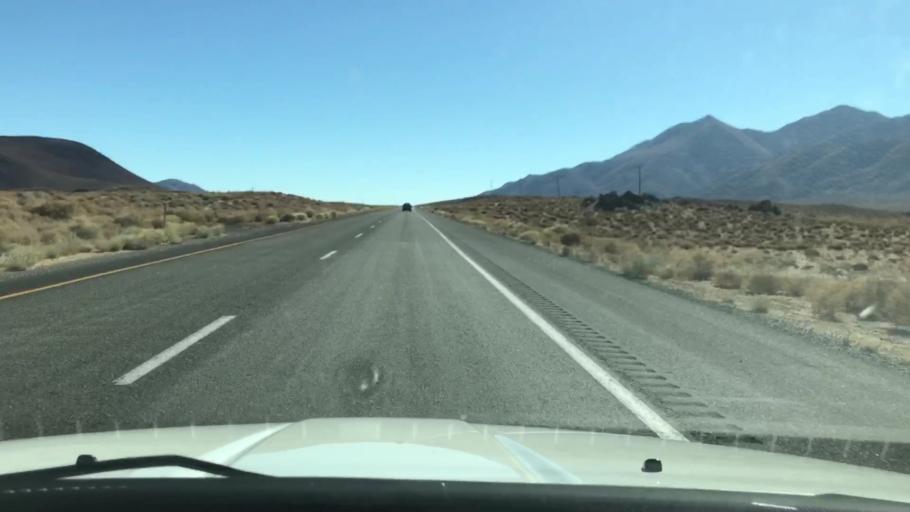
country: US
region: California
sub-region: Kern County
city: Inyokern
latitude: 36.0054
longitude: -117.9352
